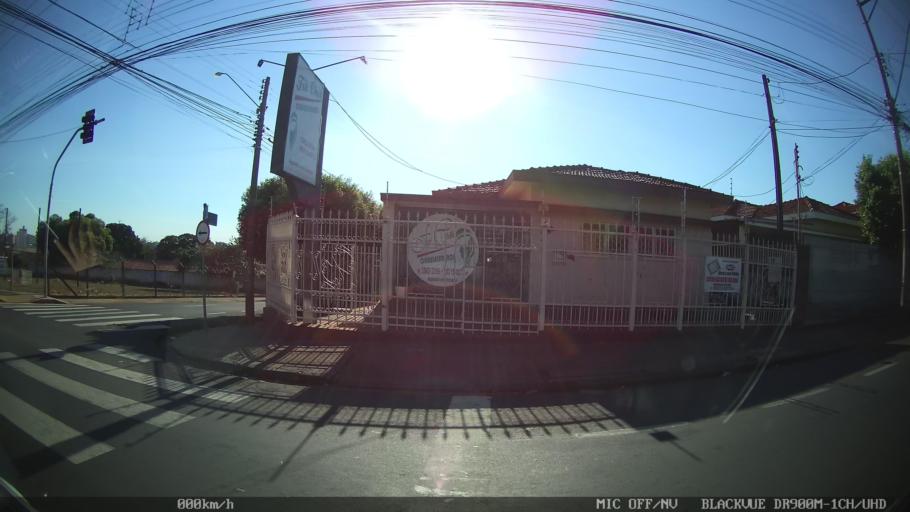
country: BR
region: Sao Paulo
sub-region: Sao Jose Do Rio Preto
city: Sao Jose do Rio Preto
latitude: -20.8009
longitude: -49.3710
